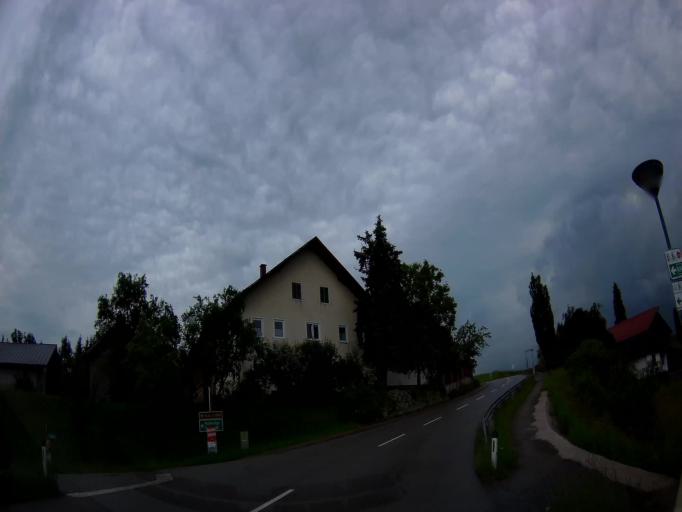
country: AT
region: Salzburg
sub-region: Politischer Bezirk Salzburg-Umgebung
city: Mattsee
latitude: 48.0472
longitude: 13.1501
